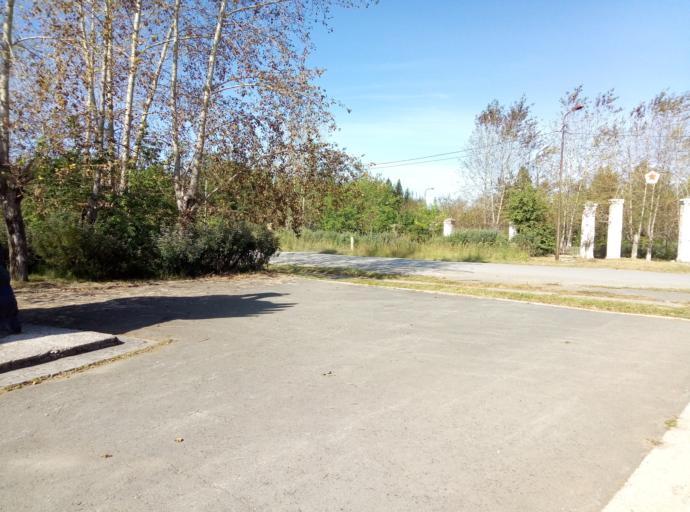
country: RU
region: Sverdlovsk
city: Karpinsk
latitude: 59.7720
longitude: 59.9872
